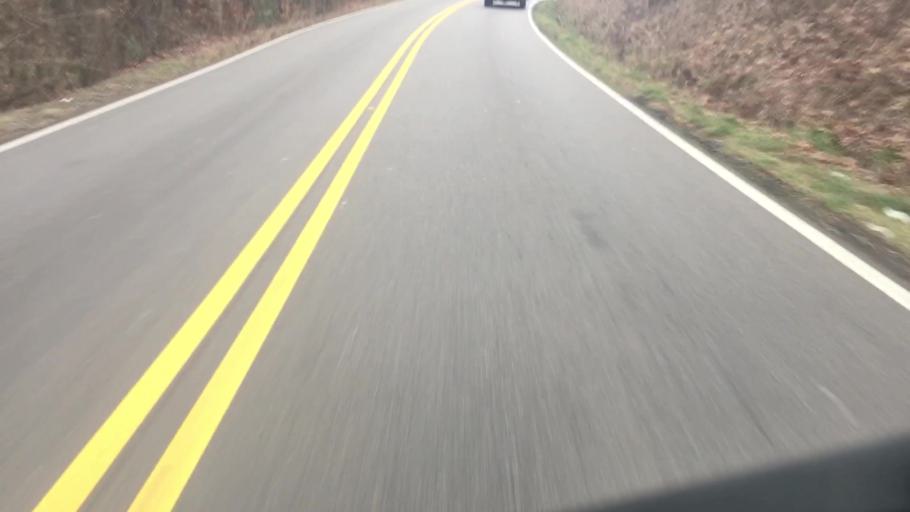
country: US
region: Alabama
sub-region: Jefferson County
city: Cahaba Heights
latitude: 33.4602
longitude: -86.7591
